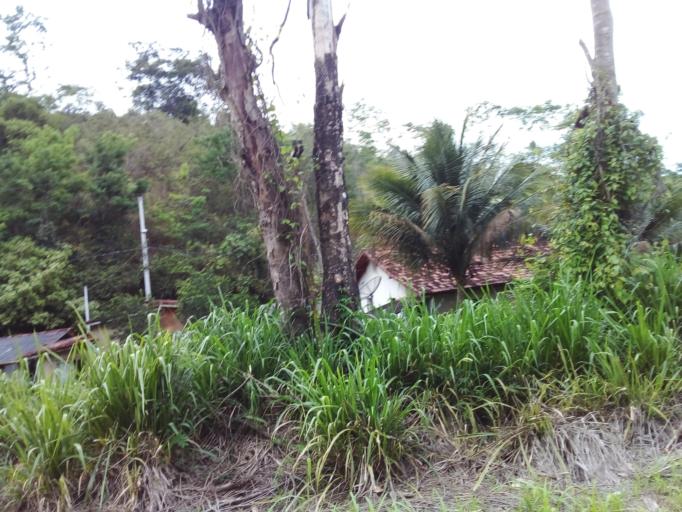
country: BR
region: Espirito Santo
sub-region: Joao Neiva
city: Joao Neiva
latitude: -19.6907
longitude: -40.3942
